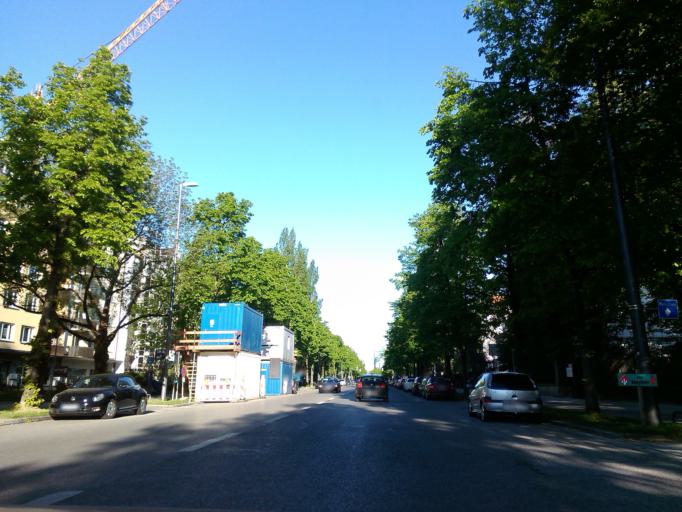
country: DE
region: Bavaria
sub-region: Upper Bavaria
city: Munich
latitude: 48.1490
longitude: 11.5503
